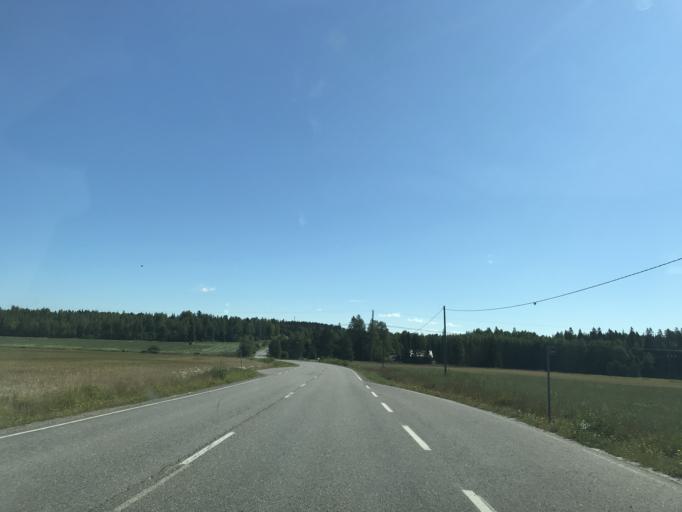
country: FI
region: Paijanne Tavastia
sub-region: Lahti
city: Orimattila
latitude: 60.8097
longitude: 25.7002
